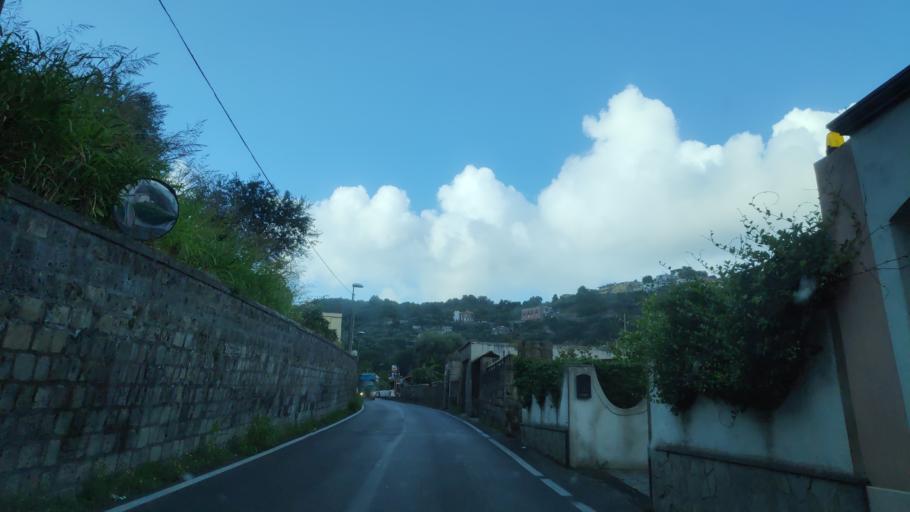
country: IT
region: Campania
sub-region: Provincia di Napoli
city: Piano di Sorrento
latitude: 40.6247
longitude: 14.4237
